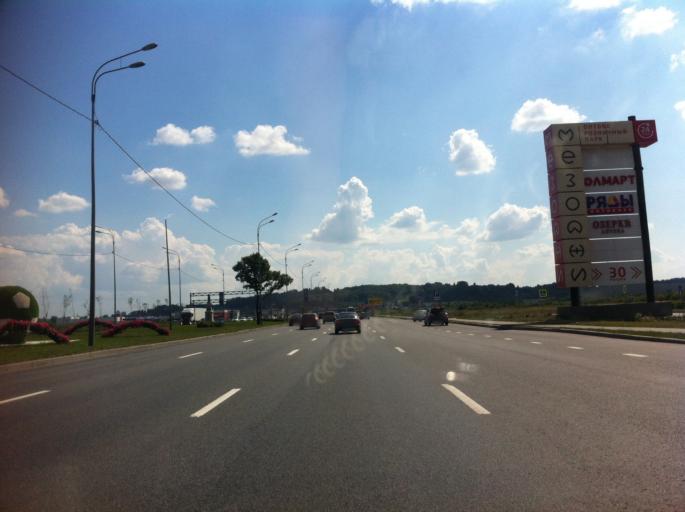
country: RU
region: St.-Petersburg
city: Aleksandrovskaya
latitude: 59.7885
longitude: 30.3246
